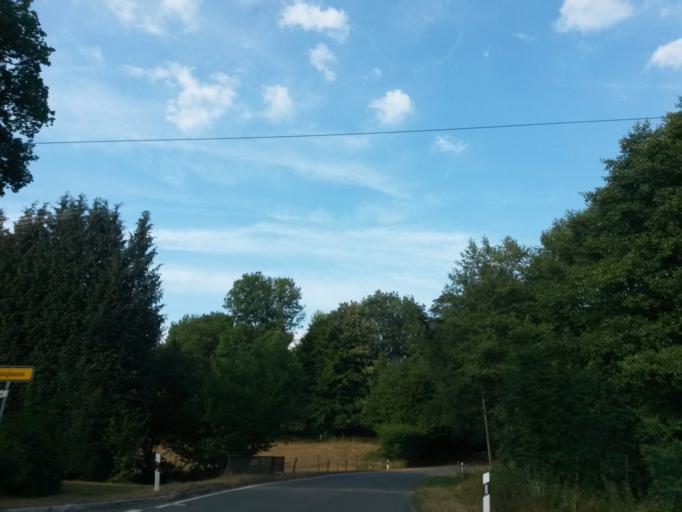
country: DE
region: North Rhine-Westphalia
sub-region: Regierungsbezirk Koln
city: Marienheide
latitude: 51.0615
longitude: 7.5284
